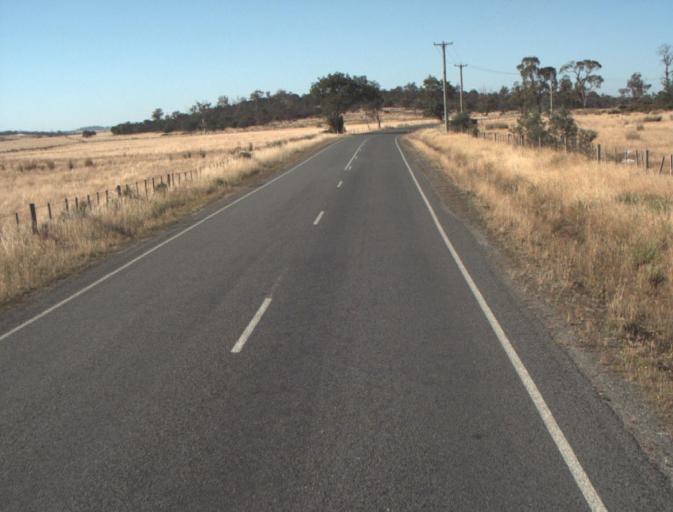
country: AU
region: Tasmania
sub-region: Launceston
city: Newstead
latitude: -41.4394
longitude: 147.2546
